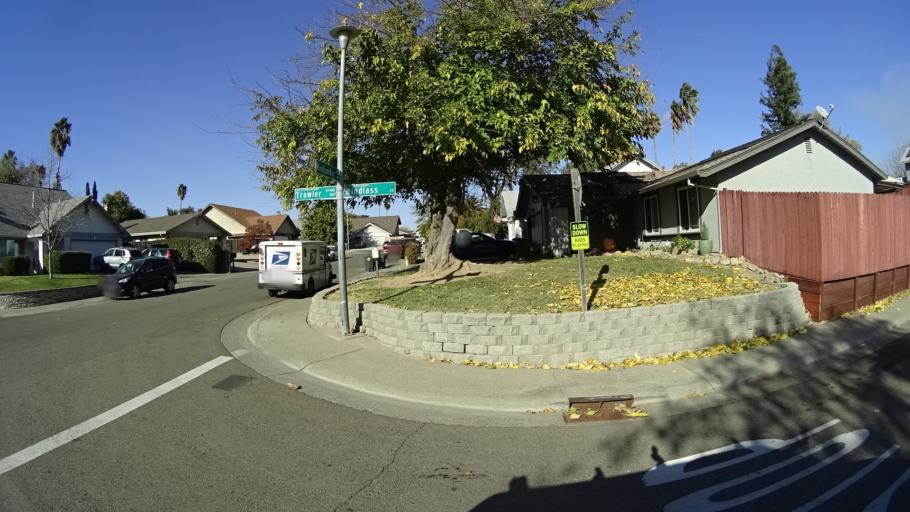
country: US
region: California
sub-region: Sacramento County
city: Antelope
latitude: 38.7003
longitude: -121.3242
